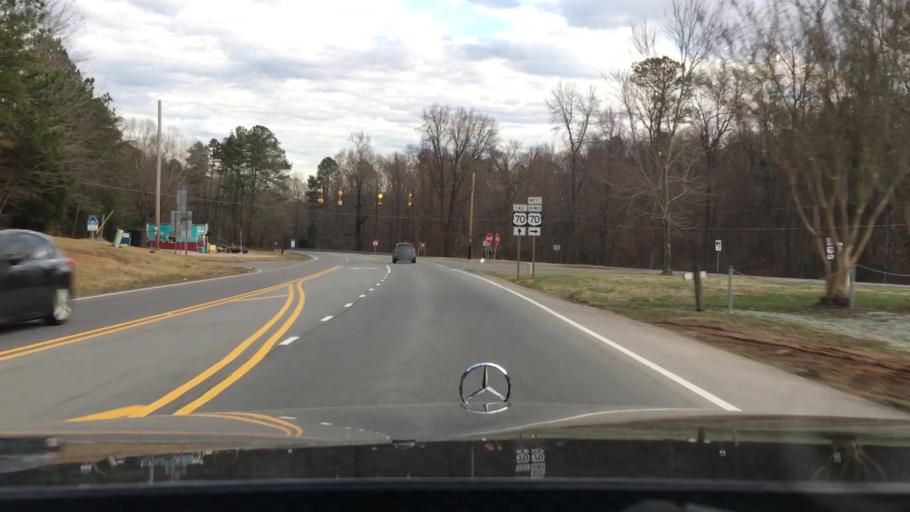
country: US
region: North Carolina
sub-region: Orange County
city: Hillsborough
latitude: 36.0567
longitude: -79.0502
